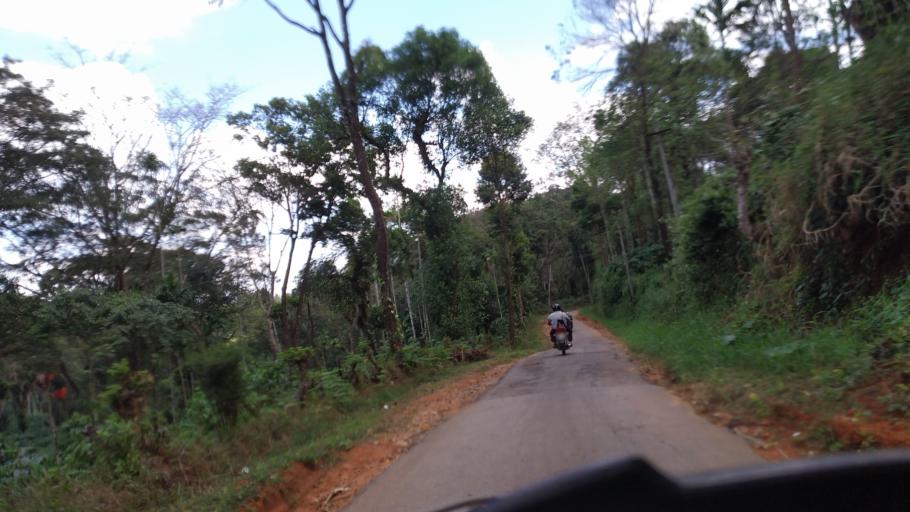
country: IN
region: Karnataka
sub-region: Kodagu
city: Ponnampet
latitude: 12.0374
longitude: 75.9088
